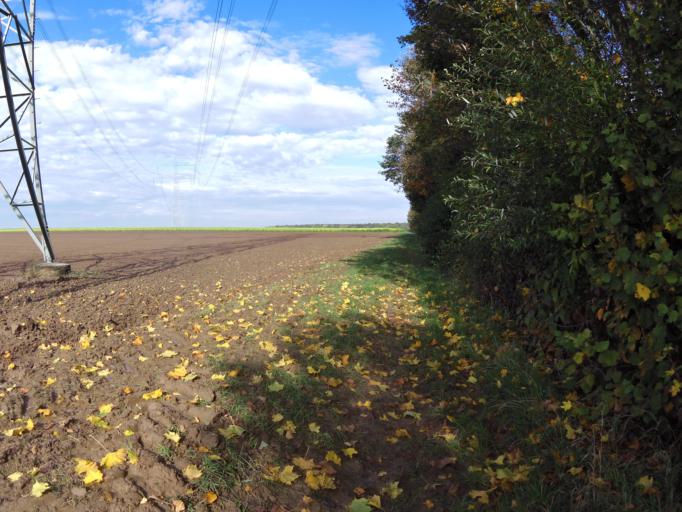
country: DE
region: Bavaria
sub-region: Regierungsbezirk Unterfranken
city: Sommerhausen
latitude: 49.7167
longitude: 10.0577
